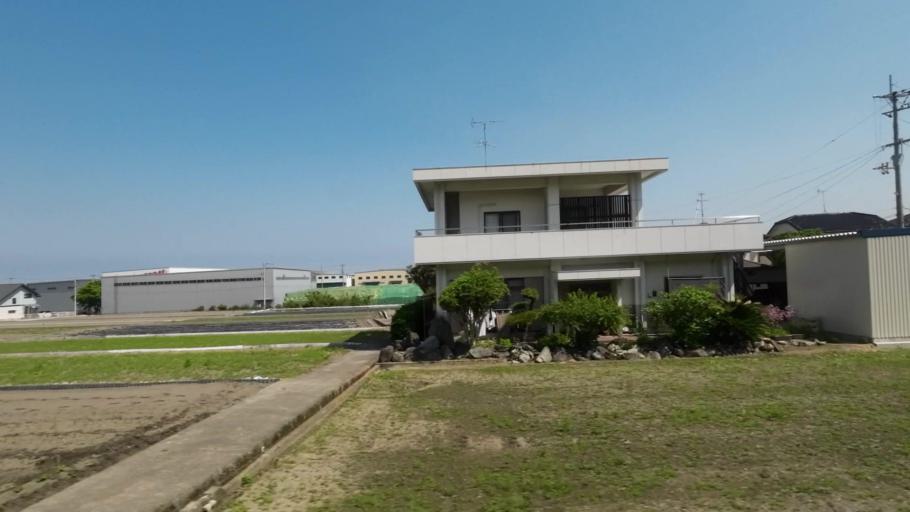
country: JP
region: Ehime
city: Kawanoecho
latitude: 33.9681
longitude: 133.5053
